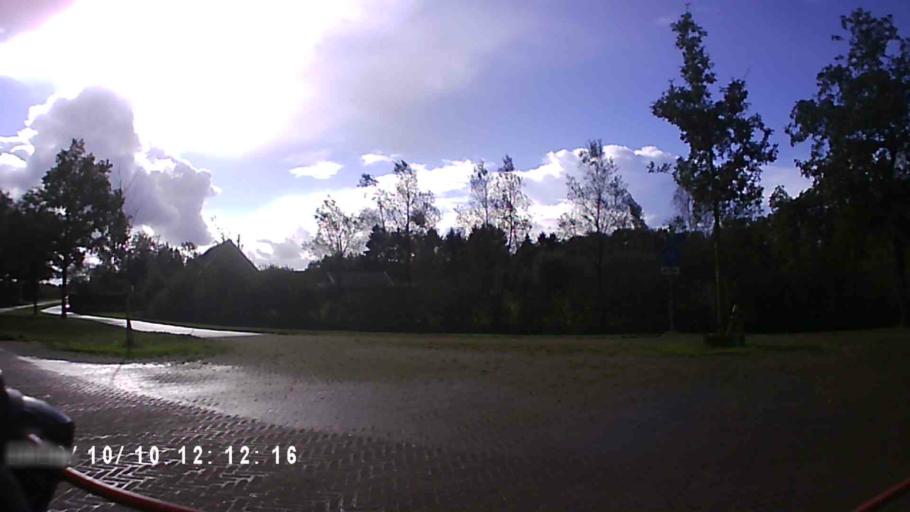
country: NL
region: Friesland
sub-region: Gemeente Heerenveen
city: Jubbega
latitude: 53.0369
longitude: 6.1527
